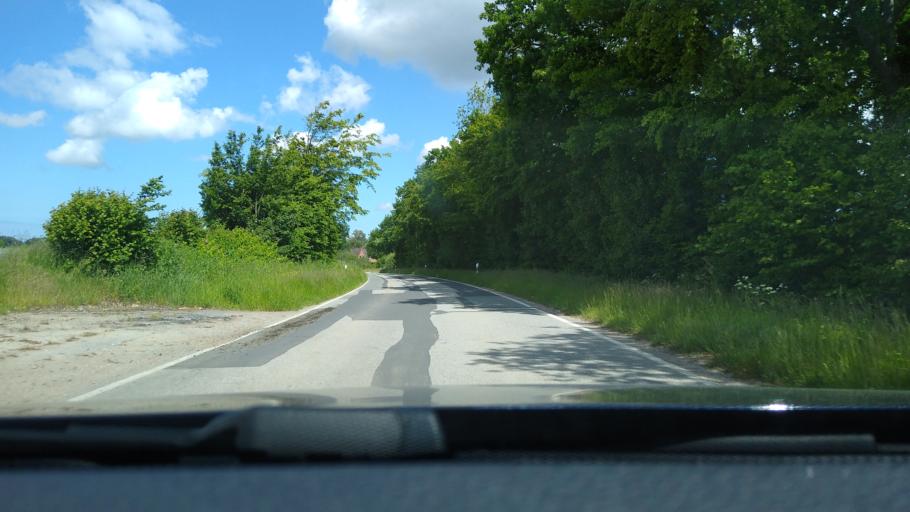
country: DE
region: Schleswig-Holstein
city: Kabelhorst
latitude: 54.2191
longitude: 10.9320
